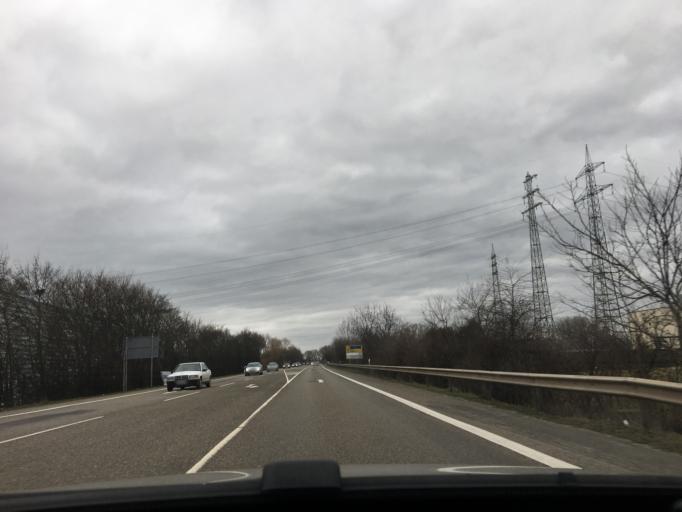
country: DE
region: Rheinland-Pfalz
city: Worms
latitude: 49.6684
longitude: 8.3549
